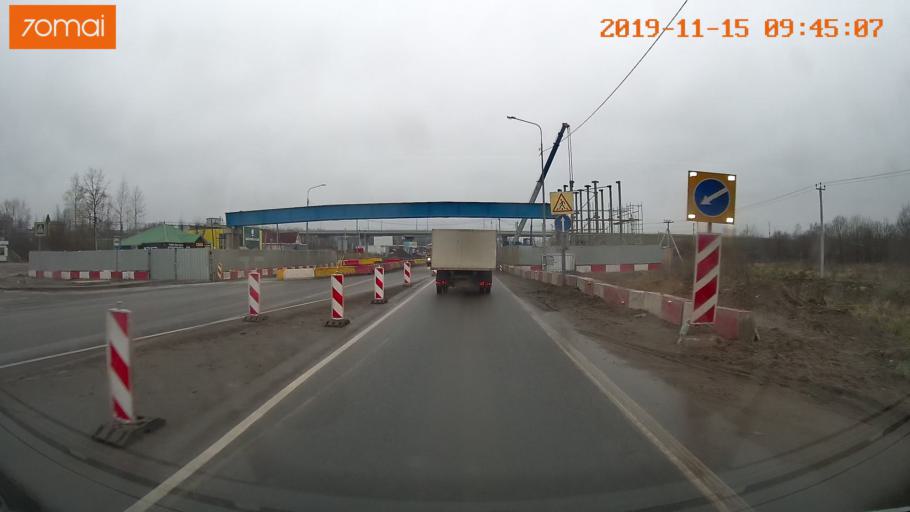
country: RU
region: Vologda
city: Sheksna
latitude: 59.2114
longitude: 38.5206
